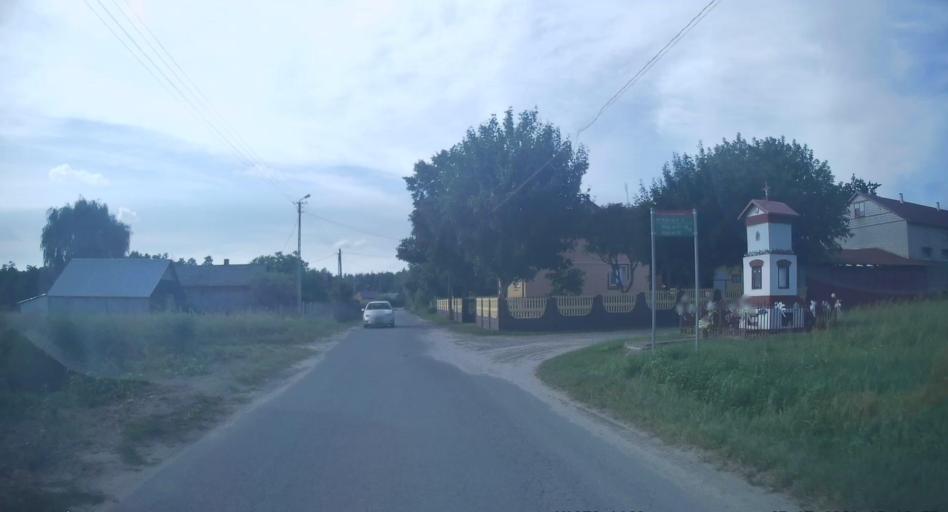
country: PL
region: Lodz Voivodeship
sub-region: Powiat rawski
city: Rawa Mazowiecka
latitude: 51.6934
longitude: 20.2537
